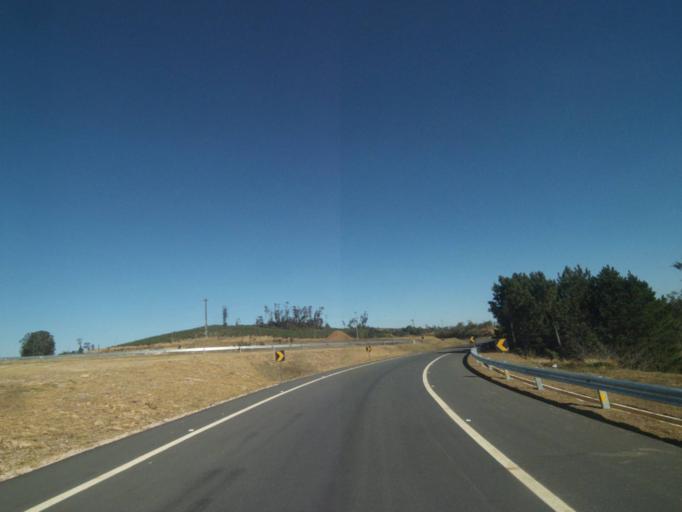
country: BR
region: Parana
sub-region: Tibagi
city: Tibagi
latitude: -24.8145
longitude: -50.4879
